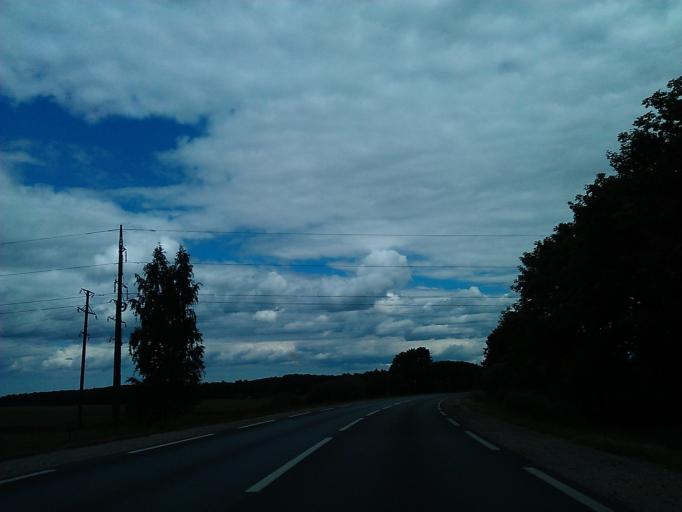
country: LV
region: Dobeles Rajons
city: Dobele
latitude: 56.6300
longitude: 23.3010
